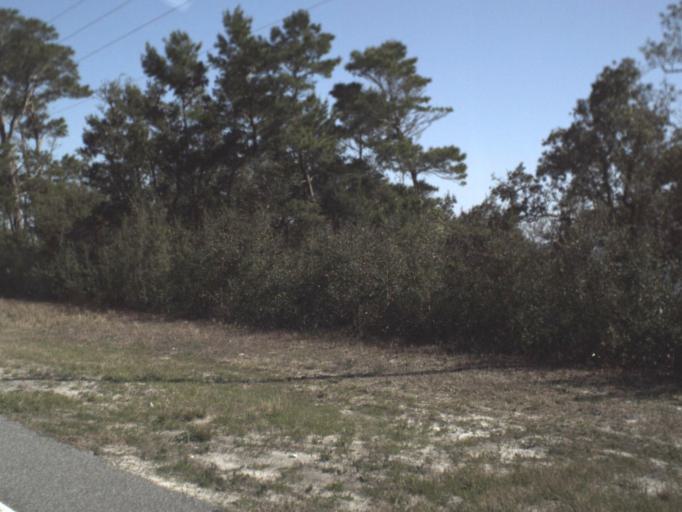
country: US
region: Florida
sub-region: Franklin County
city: Carrabelle
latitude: 29.9256
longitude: -84.4212
